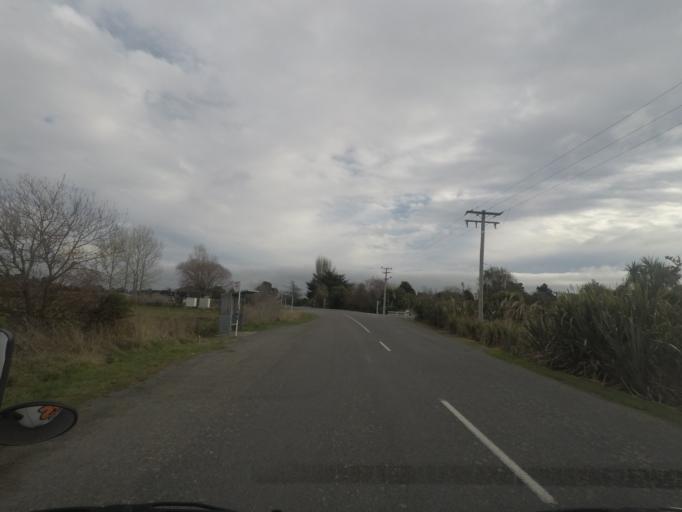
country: NZ
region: Canterbury
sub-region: Waimakariri District
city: Woodend
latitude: -43.2872
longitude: 172.7111
